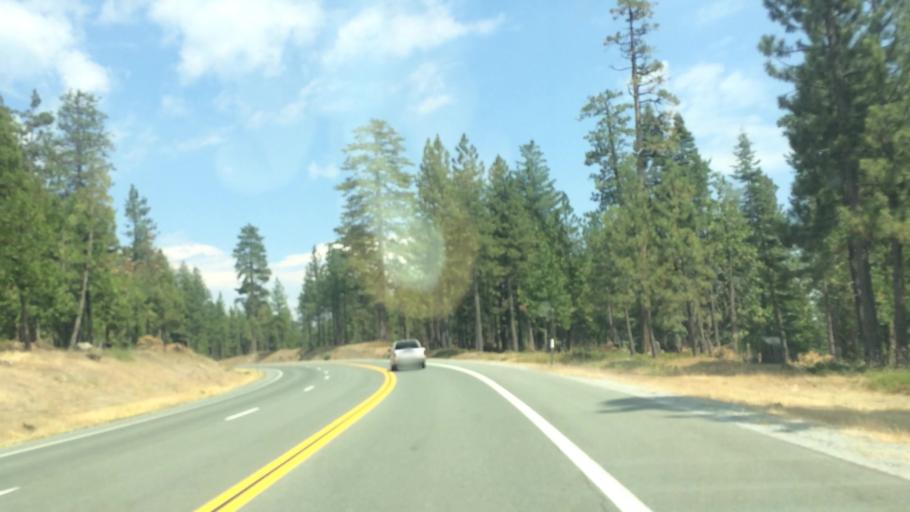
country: US
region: California
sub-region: Amador County
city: Pioneer
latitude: 38.5309
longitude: -120.4153
